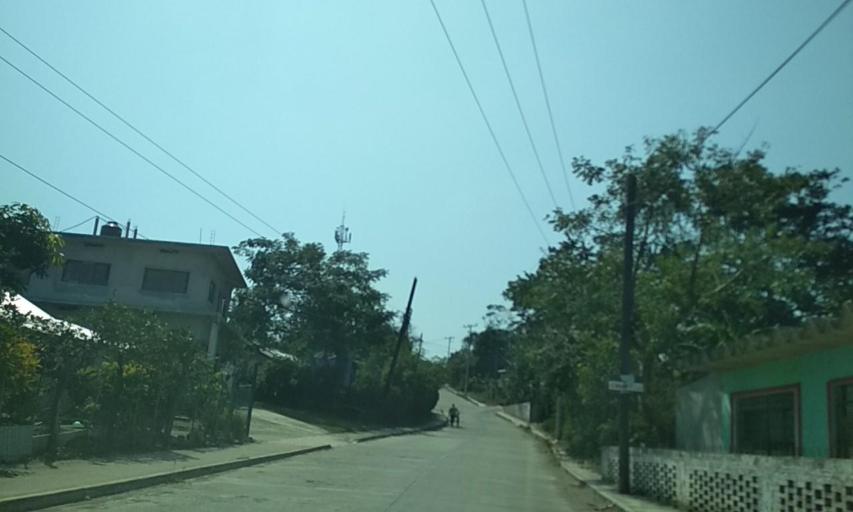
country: MX
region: Veracruz
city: Gutierrez Zamora
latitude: 20.4212
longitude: -97.1867
